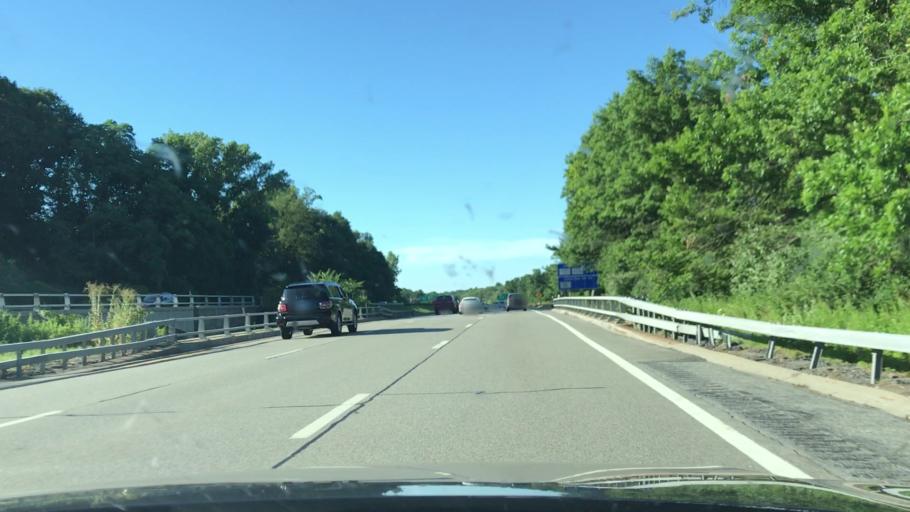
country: US
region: New York
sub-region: Westchester County
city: Jefferson Valley-Yorktown
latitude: 41.2834
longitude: -73.8199
